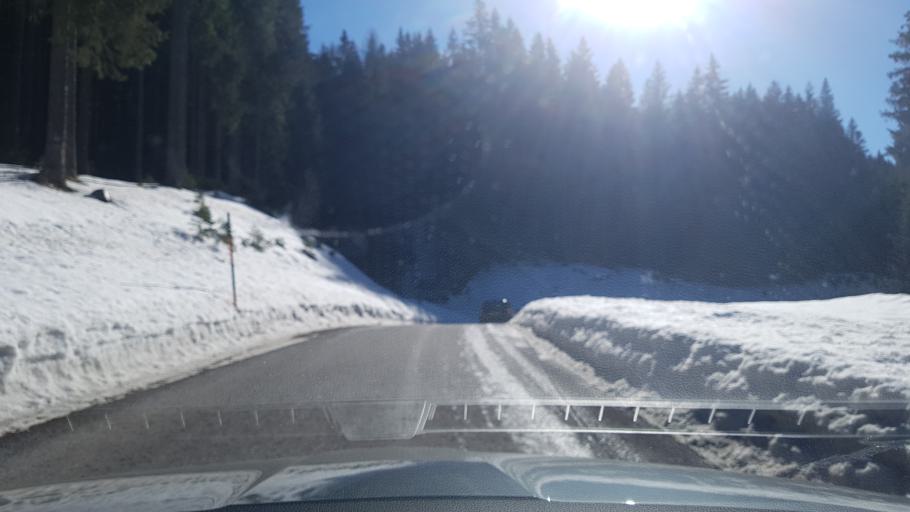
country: AT
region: Salzburg
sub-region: Politischer Bezirk Hallein
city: Abtenau
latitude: 47.6361
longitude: 13.4175
